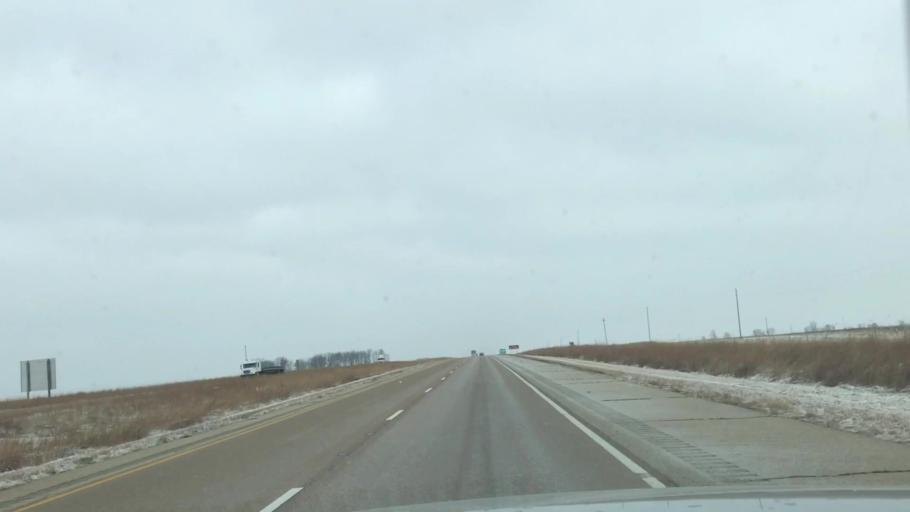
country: US
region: Illinois
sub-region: Montgomery County
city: Raymond
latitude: 39.2978
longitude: -89.6419
